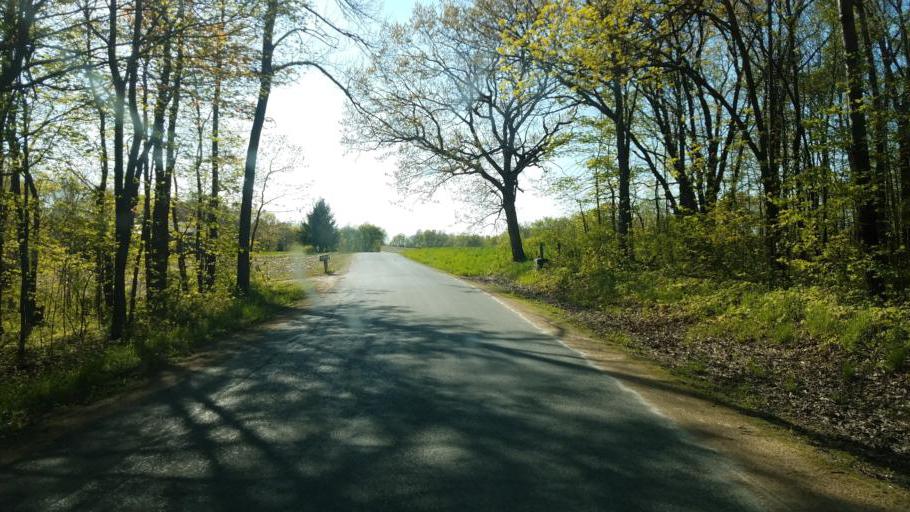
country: US
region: Wisconsin
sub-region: Vernon County
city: Hillsboro
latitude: 43.6738
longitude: -90.3568
